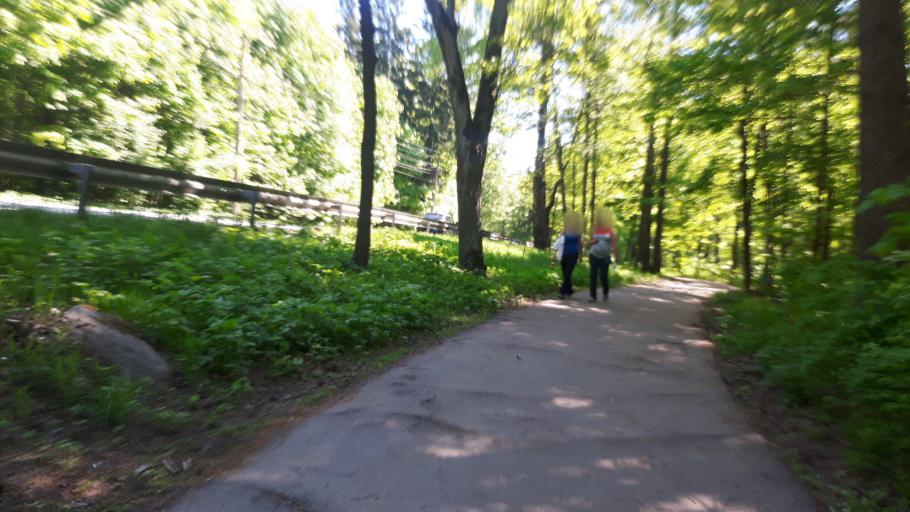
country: RU
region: St.-Petersburg
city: Zelenogorsk
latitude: 60.1929
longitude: 29.6755
